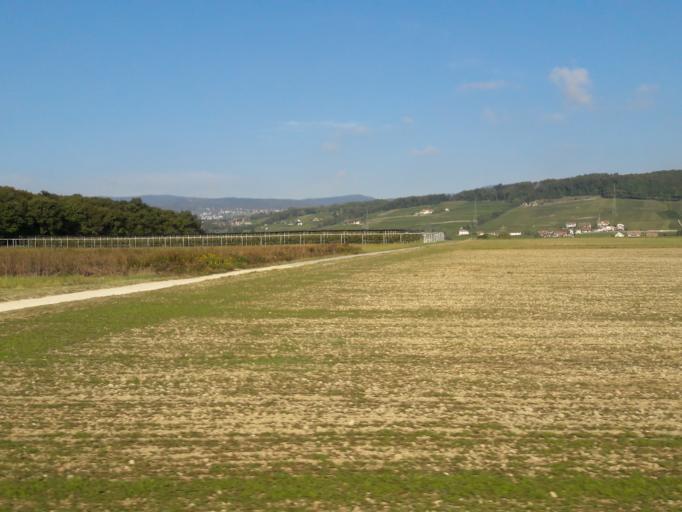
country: CH
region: Vaud
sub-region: Nyon District
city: Gland
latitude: 46.4322
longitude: 6.2818
